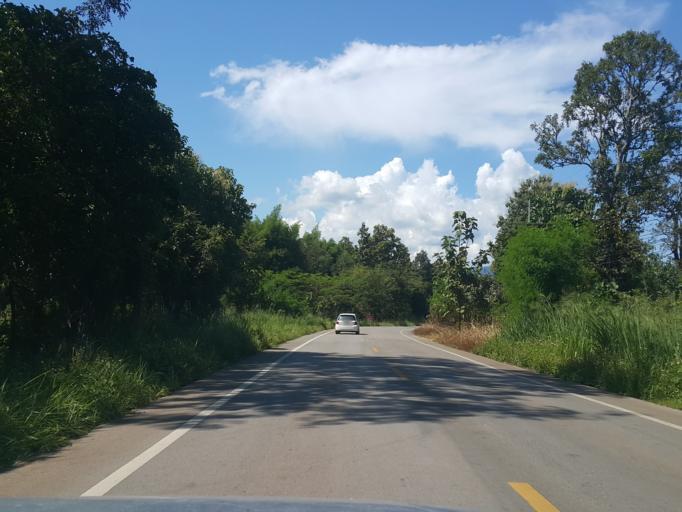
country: TH
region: Chiang Mai
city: Mae Taeng
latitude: 19.1532
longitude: 98.9437
